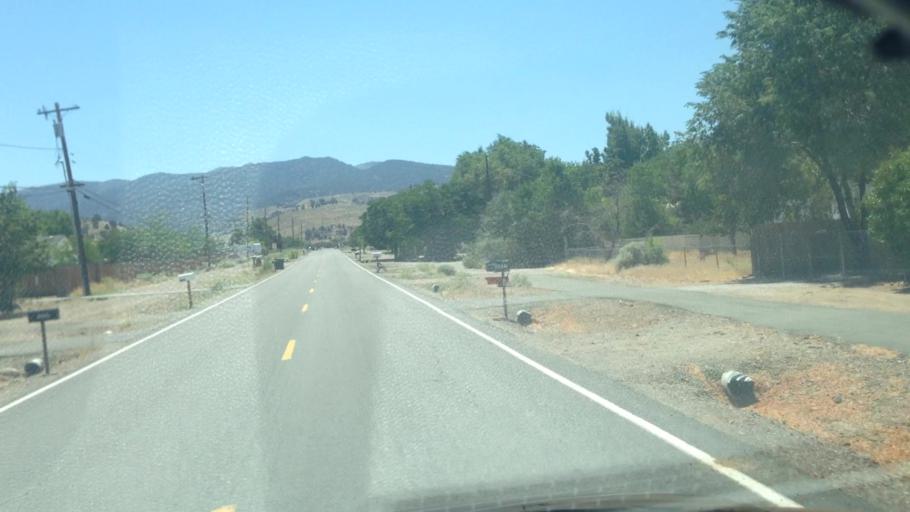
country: US
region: Nevada
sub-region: Storey County
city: Virginia City
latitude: 39.3816
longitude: -119.7218
